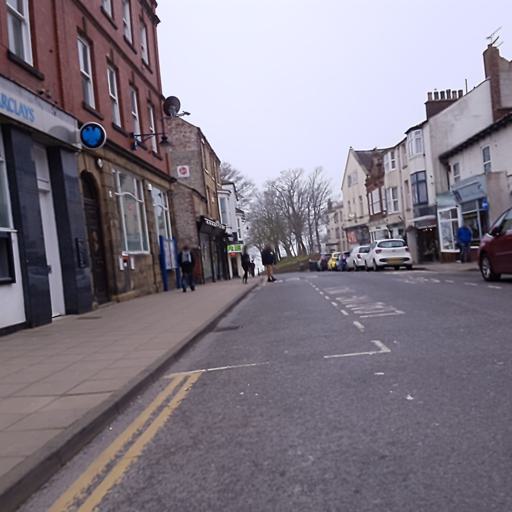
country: GB
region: England
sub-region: North Yorkshire
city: Filey
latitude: 54.2093
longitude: -0.2878
